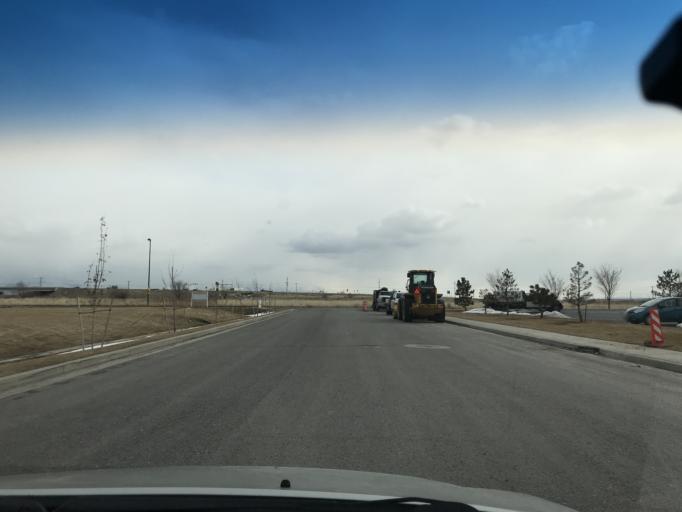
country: US
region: Utah
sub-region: Salt Lake County
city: West Valley City
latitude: 40.7731
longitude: -112.0300
